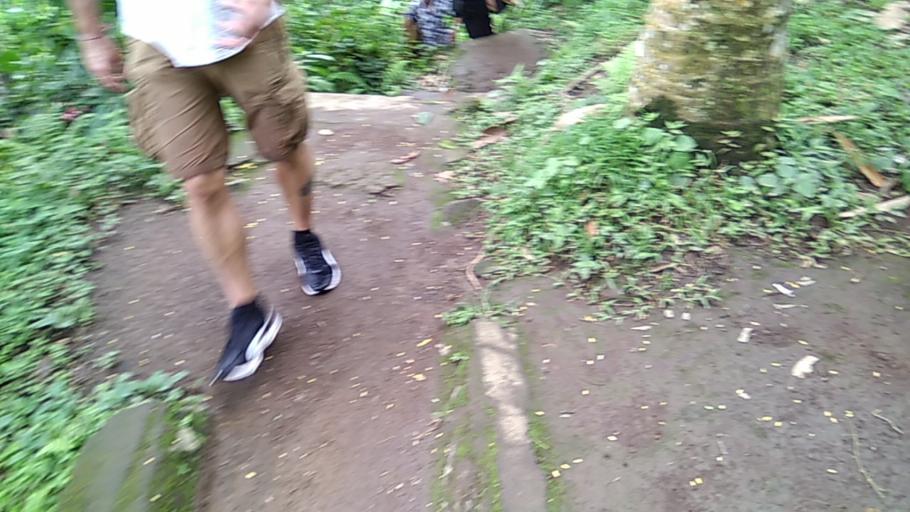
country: ID
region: Bali
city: Banjar Kubu
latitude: -8.4411
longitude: 115.3884
